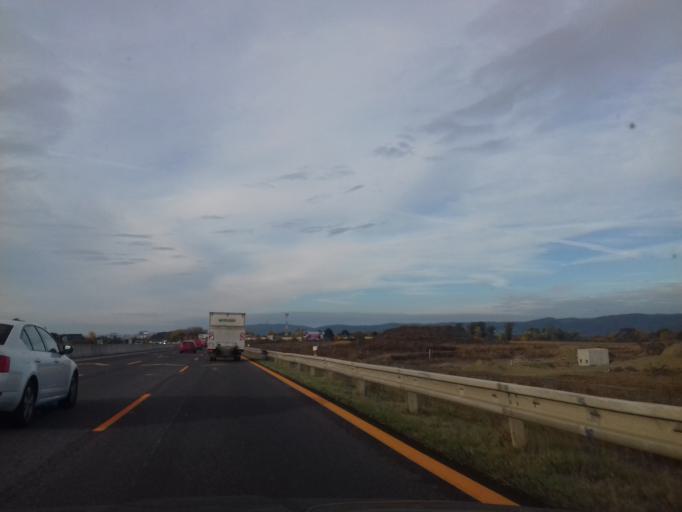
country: SK
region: Bratislavsky
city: Svaty Jur
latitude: 48.2121
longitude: 17.2586
